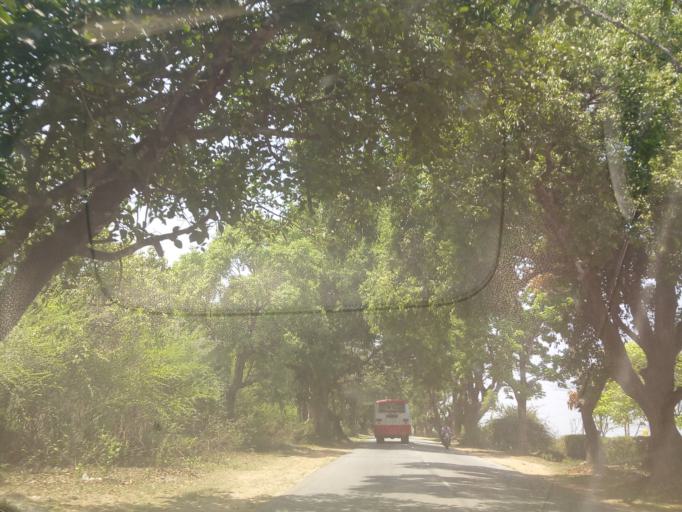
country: IN
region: Karnataka
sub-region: Hassan
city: Alur
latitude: 12.9449
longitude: 75.8995
